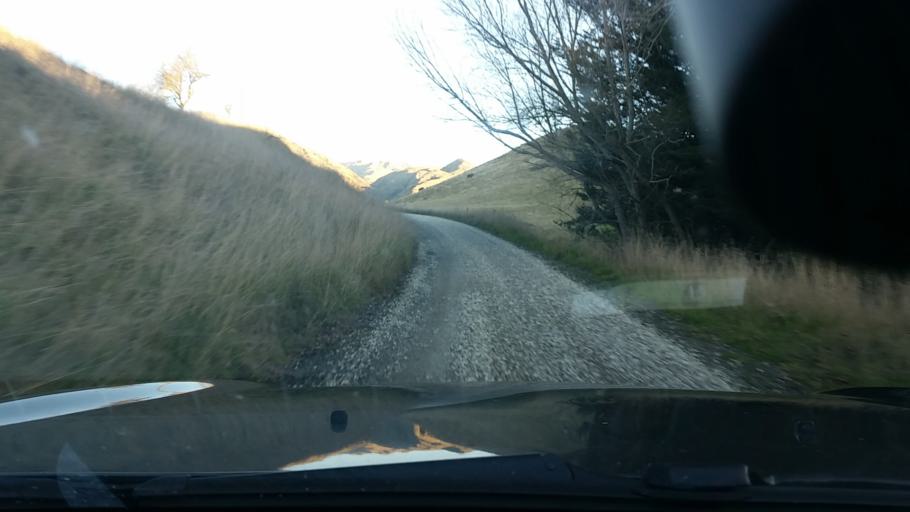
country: NZ
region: Marlborough
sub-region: Marlborough District
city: Blenheim
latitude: -41.7301
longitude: 174.0366
